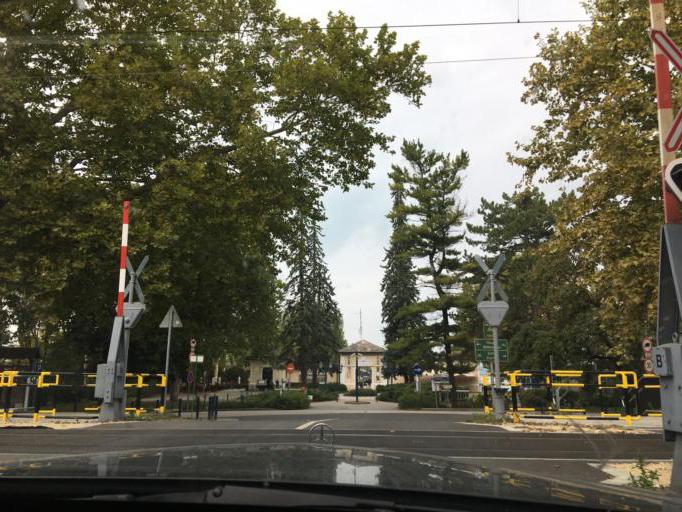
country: HU
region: Somogy
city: Balatonfoldvar
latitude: 46.8542
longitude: 17.8820
